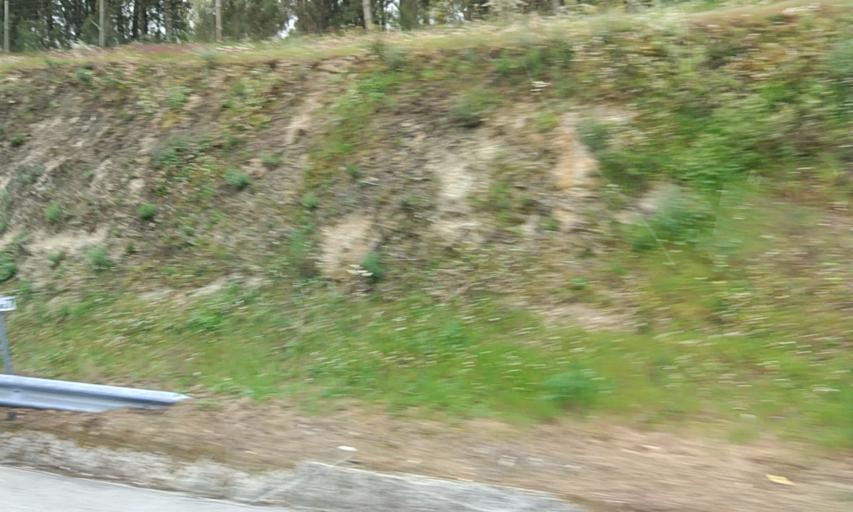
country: PT
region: Guarda
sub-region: Celorico da Beira
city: Celorico da Beira
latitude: 40.6278
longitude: -7.3844
